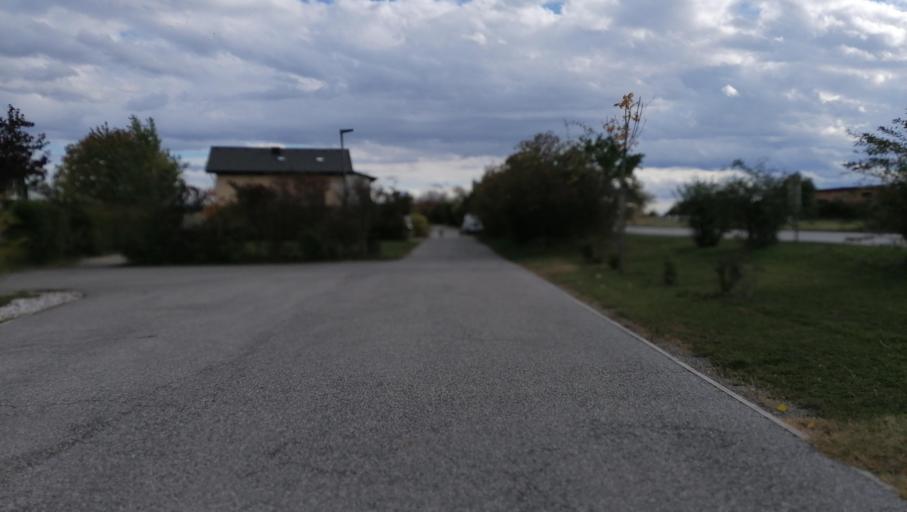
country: AT
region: Lower Austria
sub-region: Politischer Bezirk Baden
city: Tattendorf
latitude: 47.9538
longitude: 16.3049
